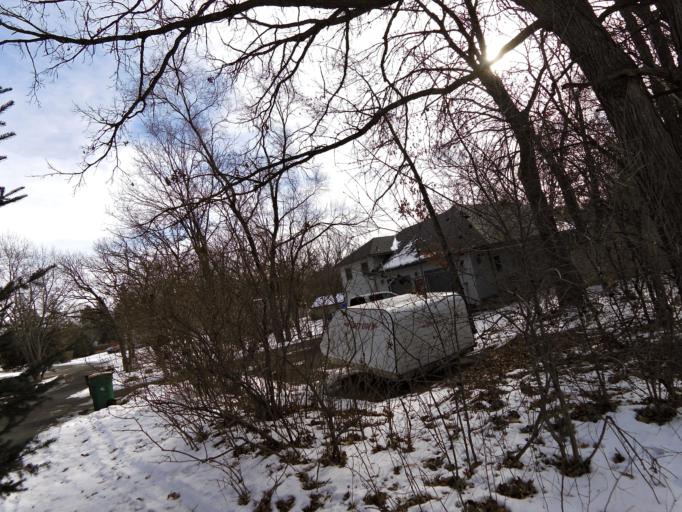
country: US
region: Minnesota
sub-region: Washington County
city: Lake Saint Croix Beach
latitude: 44.9169
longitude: -92.7749
